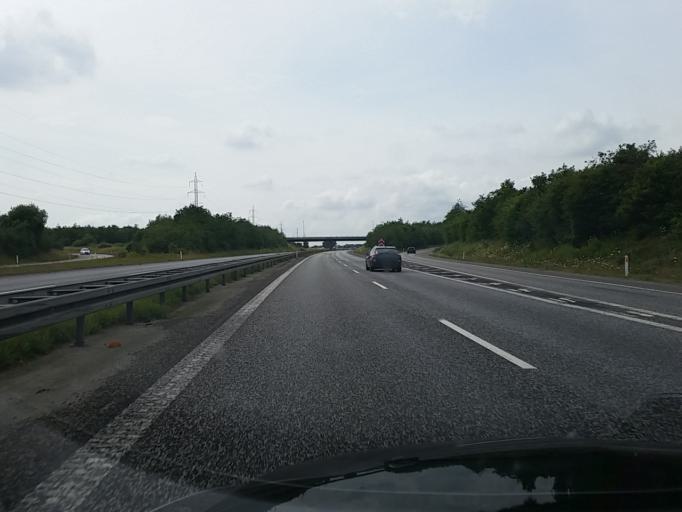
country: DK
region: South Denmark
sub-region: Kolding Kommune
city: Lunderskov
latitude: 55.5073
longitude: 9.3303
